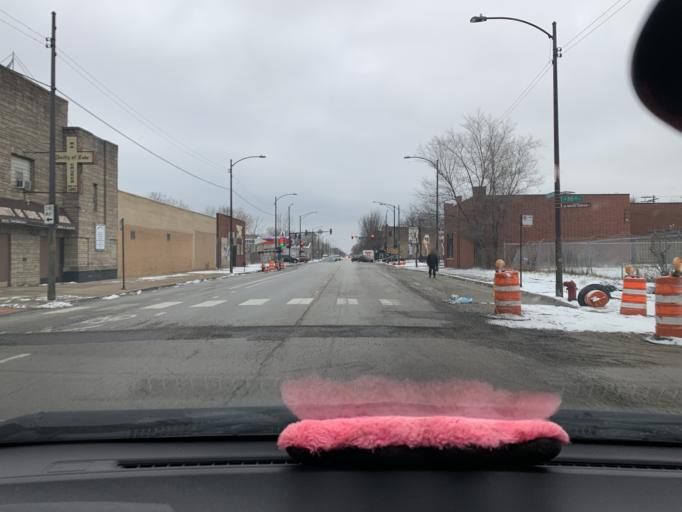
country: US
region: Illinois
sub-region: Cook County
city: Chicago
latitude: 41.8025
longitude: -87.6454
